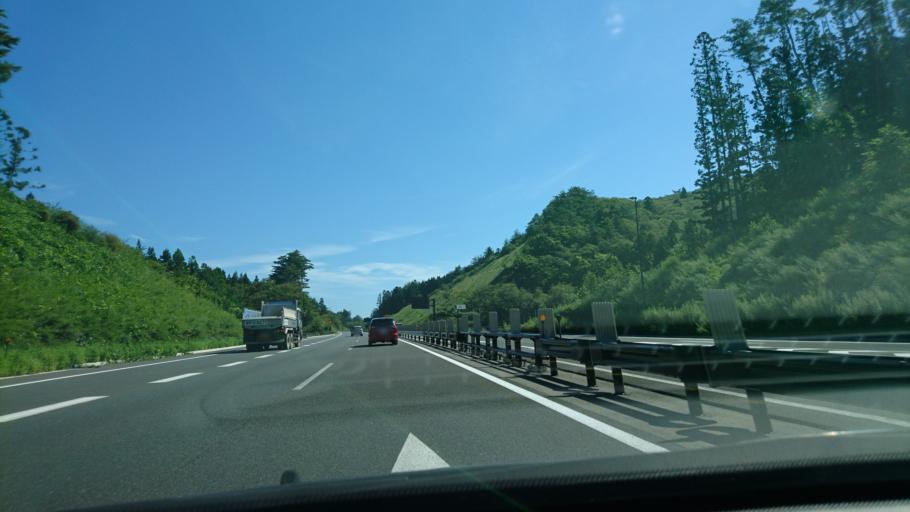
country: JP
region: Iwate
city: Tono
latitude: 39.2951
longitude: 141.4078
